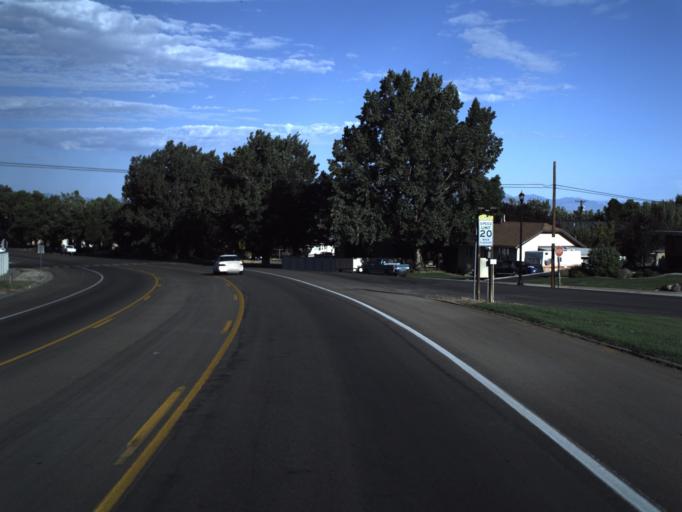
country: US
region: Utah
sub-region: Utah County
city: Spanish Fork
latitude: 40.1055
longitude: -111.6428
